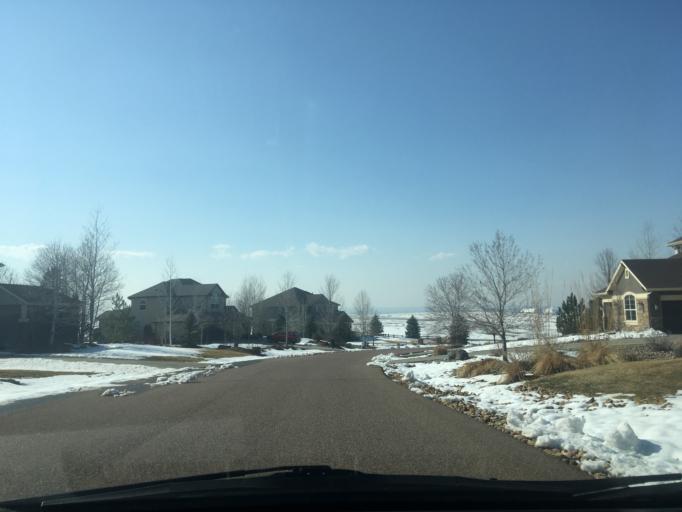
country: US
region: Colorado
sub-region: Boulder County
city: Lafayette
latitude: 39.9689
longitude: -105.0540
